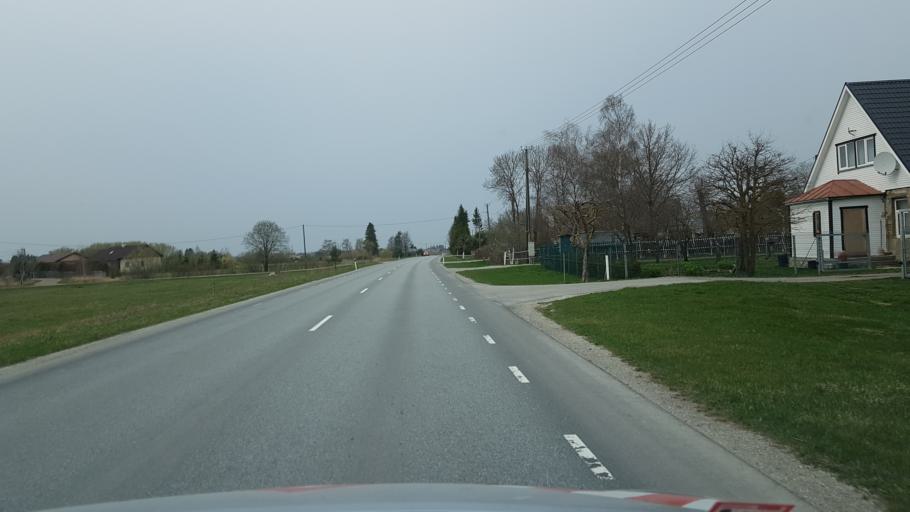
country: EE
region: Harju
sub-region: Joelaehtme vald
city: Loo
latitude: 59.3970
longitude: 24.9615
